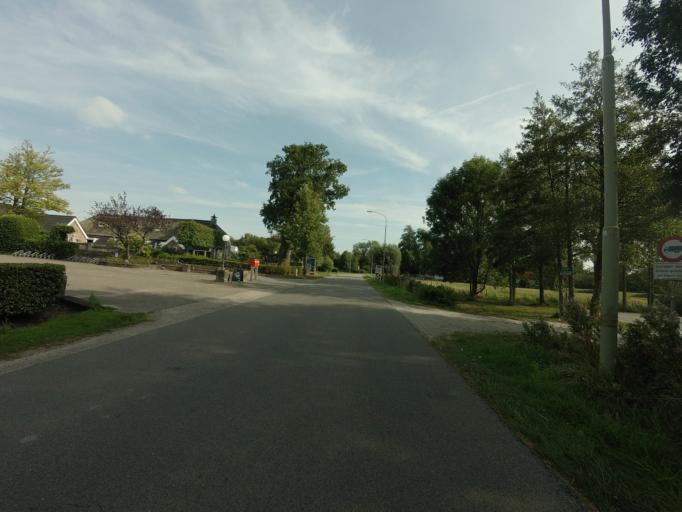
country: NL
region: Drenthe
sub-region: Gemeente Tynaarlo
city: Vries
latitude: 53.1277
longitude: 6.5666
